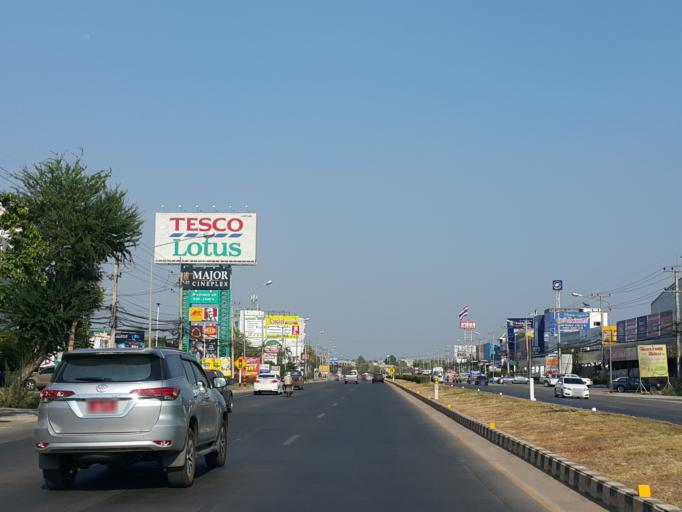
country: TH
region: Phitsanulok
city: Phitsanulok
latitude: 16.8174
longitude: 100.2991
